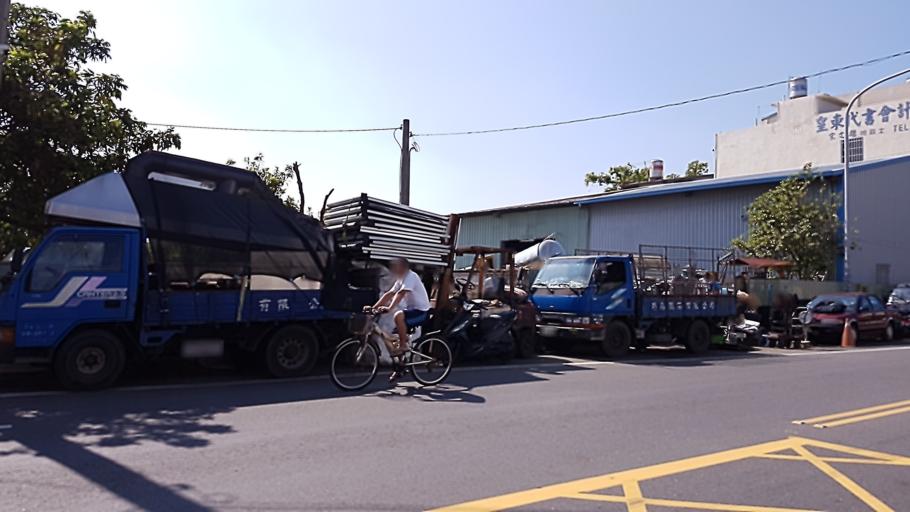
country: TW
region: Taiwan
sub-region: Changhua
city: Chang-hua
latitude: 24.0816
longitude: 120.5105
